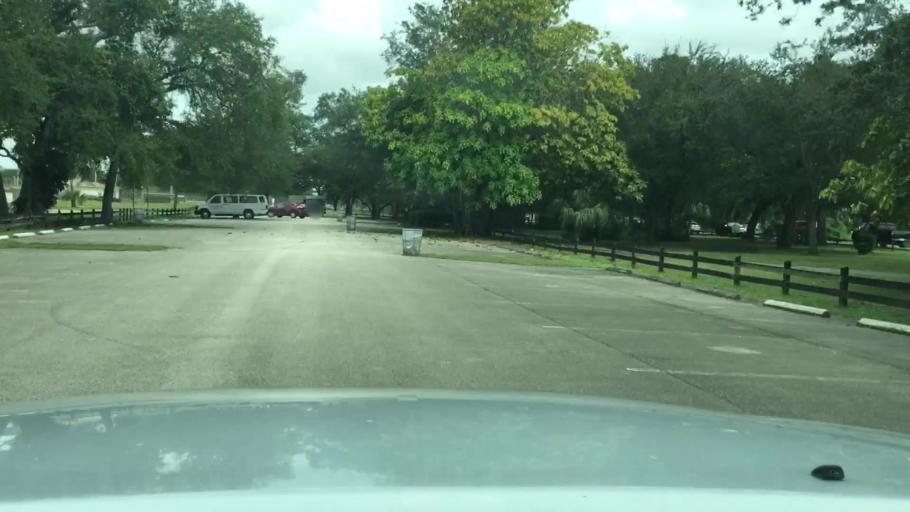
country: US
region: Florida
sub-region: Miami-Dade County
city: Sunset
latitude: 25.6933
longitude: -80.3760
